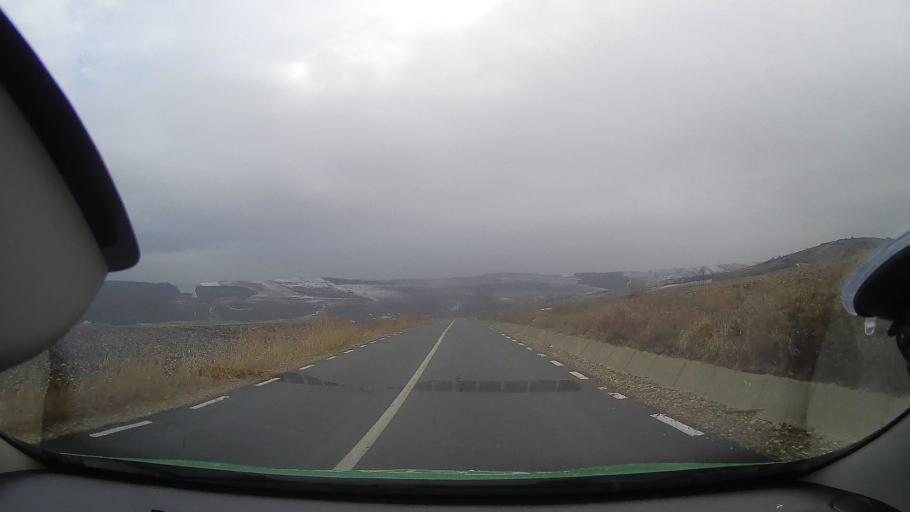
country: RO
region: Alba
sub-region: Comuna Farau
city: Farau
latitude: 46.3972
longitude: 24.0211
